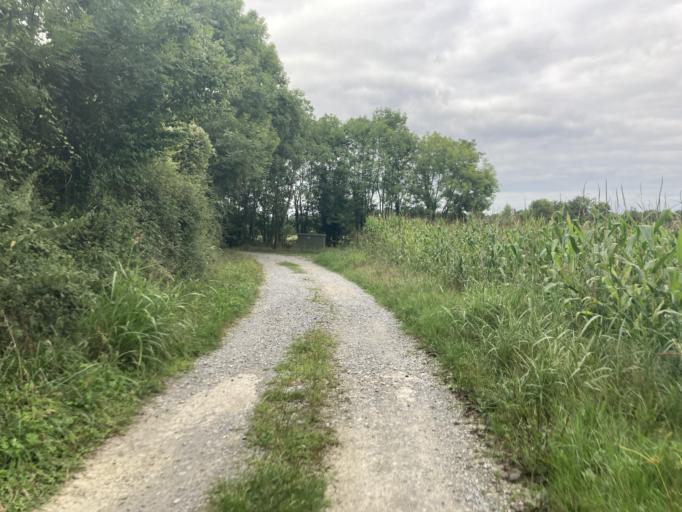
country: FR
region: Aquitaine
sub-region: Departement des Pyrenees-Atlantiques
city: Artiguelouve
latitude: 43.3251
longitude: -0.4830
